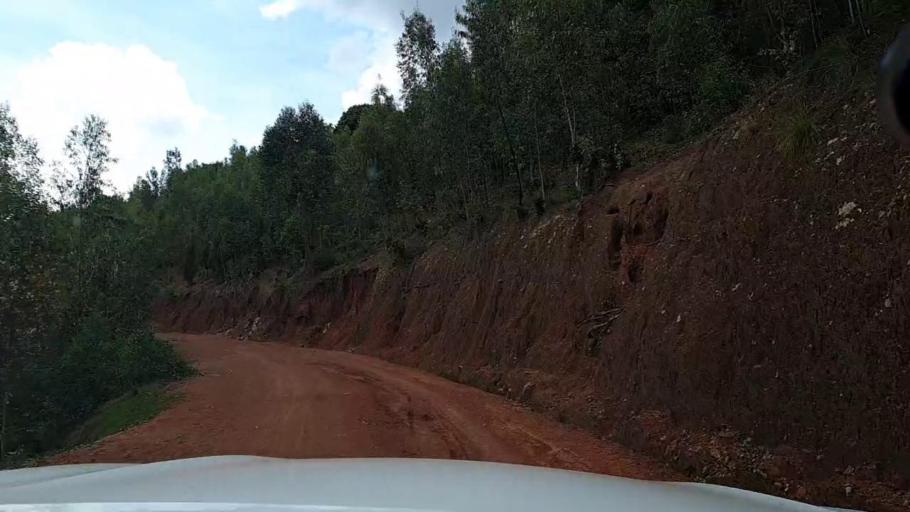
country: RW
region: Southern Province
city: Butare
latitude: -2.7546
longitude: 29.7506
